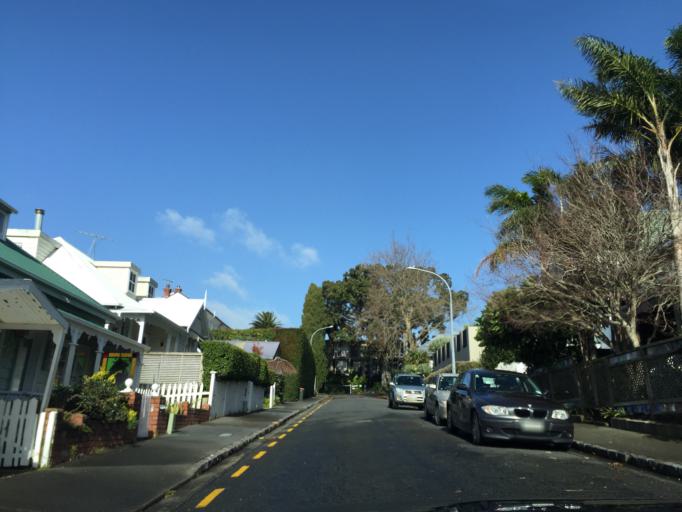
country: NZ
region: Auckland
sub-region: Auckland
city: Auckland
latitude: -36.8422
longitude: 174.7438
